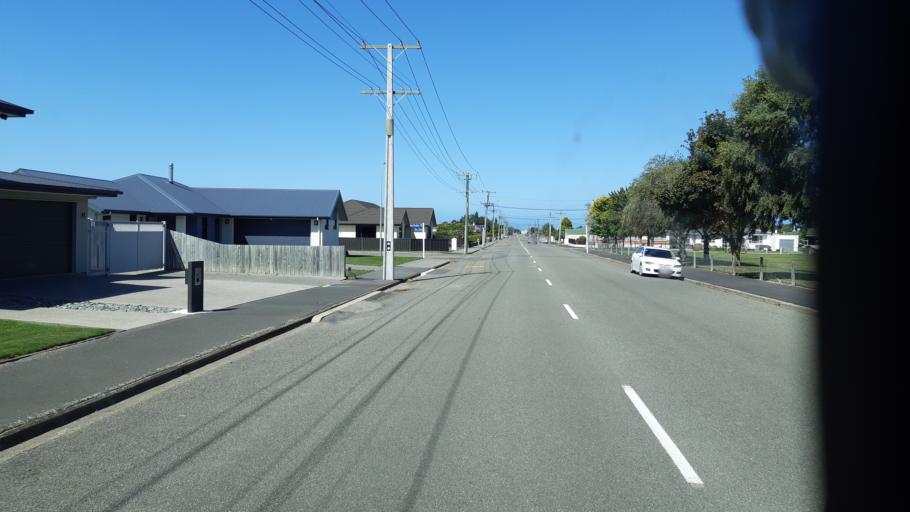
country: NZ
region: Otago
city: Oamaru
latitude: -45.0659
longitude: 170.9875
